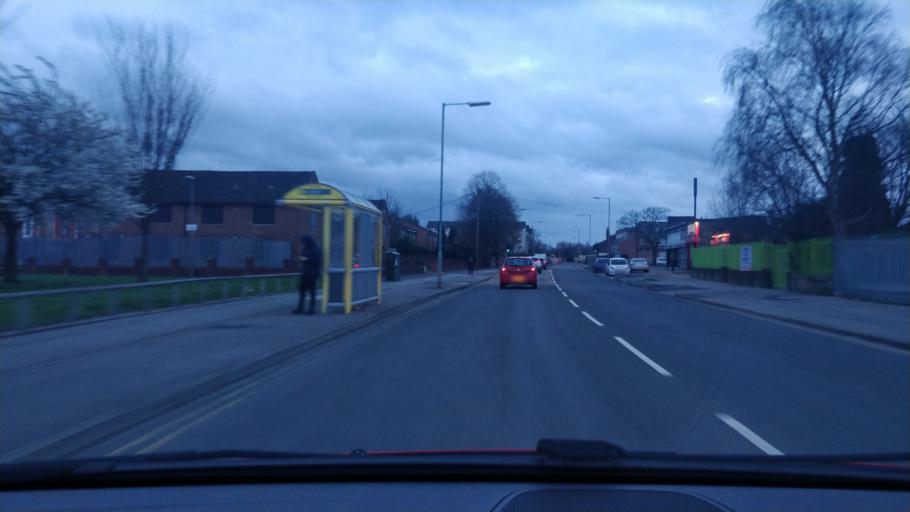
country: GB
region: England
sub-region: Knowsley
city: Kirkby
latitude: 53.4521
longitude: -2.9036
